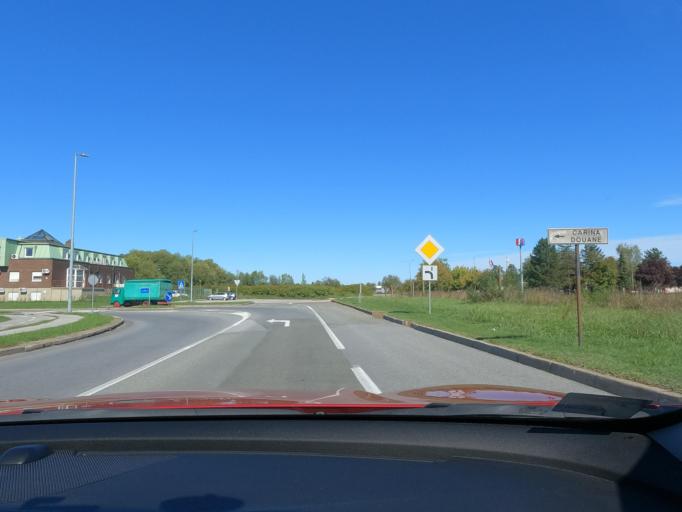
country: HR
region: Sisacko-Moslavacka
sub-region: Grad Sisak
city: Sisak
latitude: 45.4969
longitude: 16.3797
